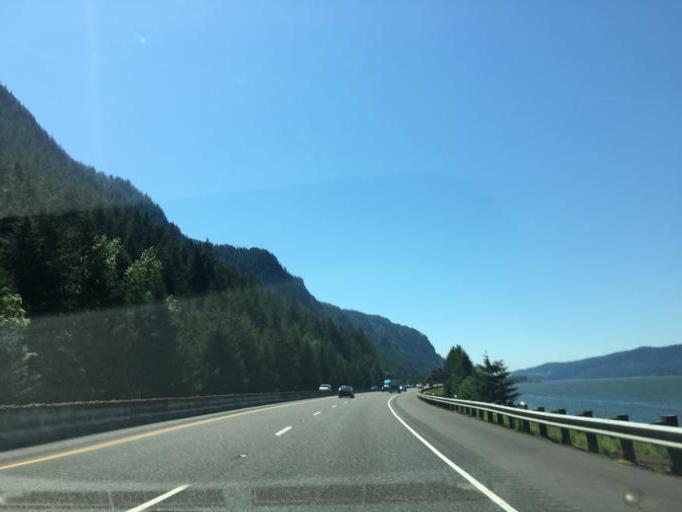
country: US
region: Oregon
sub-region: Hood River County
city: Cascade Locks
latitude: 45.5852
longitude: -122.0920
